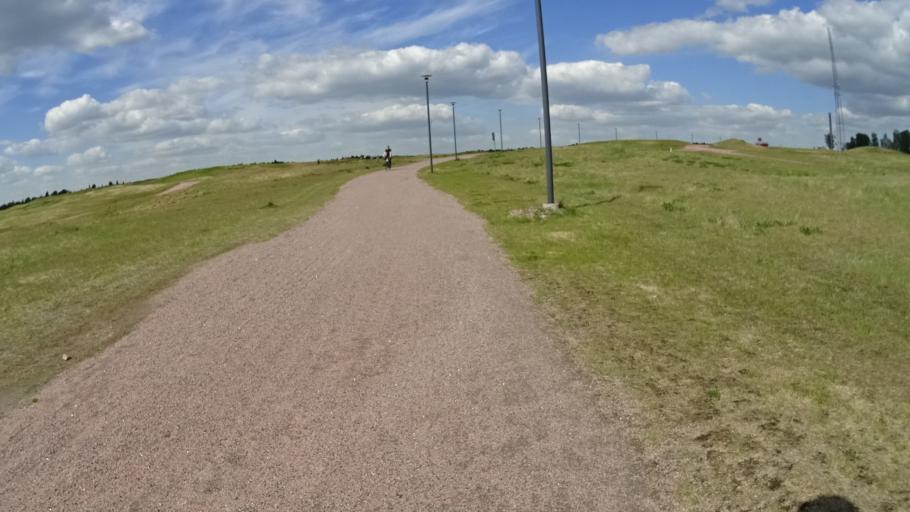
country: FI
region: Uusimaa
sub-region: Helsinki
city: Kilo
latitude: 60.1953
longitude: 24.7820
